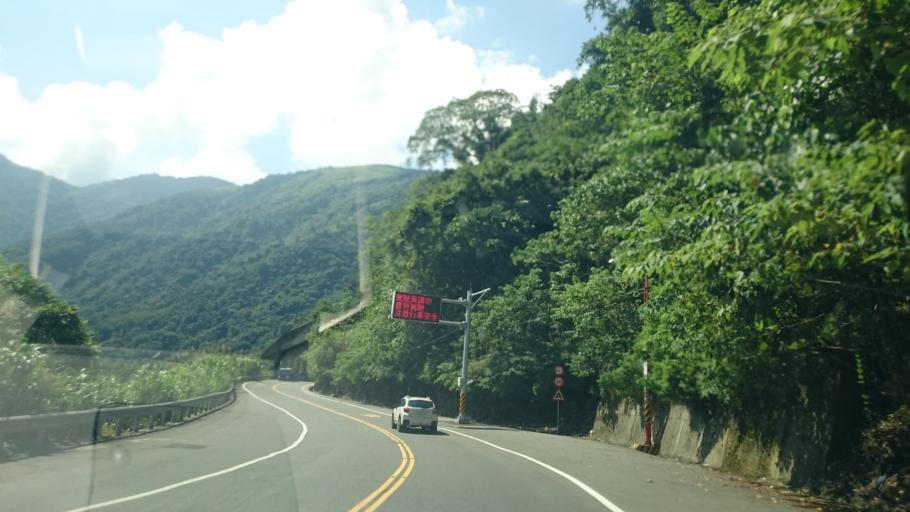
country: TW
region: Taiwan
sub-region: Nantou
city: Puli
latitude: 23.9997
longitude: 121.0668
